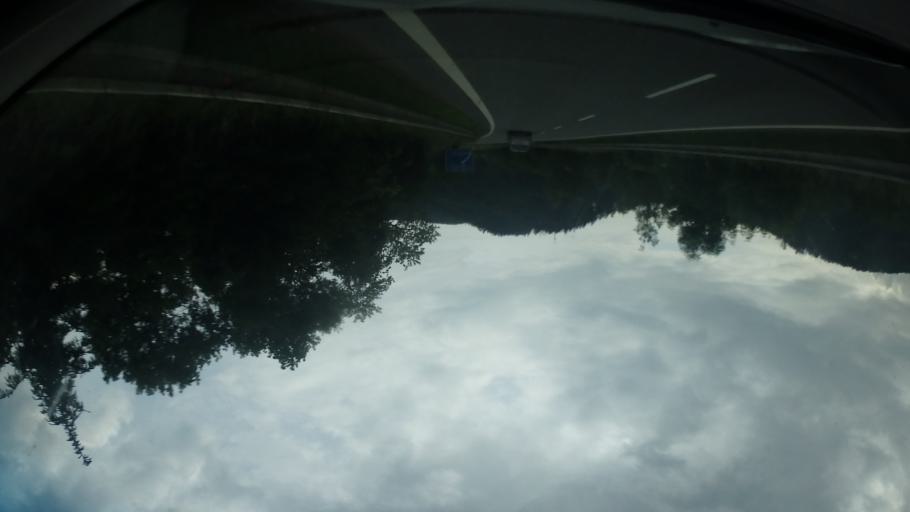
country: CZ
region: South Moravian
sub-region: Okres Brno-Venkov
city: Nedvedice
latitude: 49.4994
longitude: 16.3369
